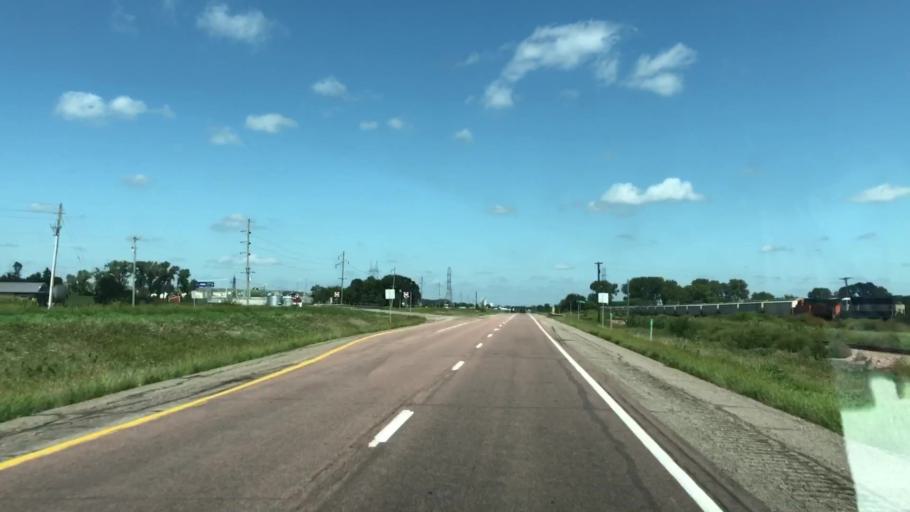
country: US
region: Iowa
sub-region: Woodbury County
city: Sioux City
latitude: 42.5926
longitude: -96.3056
